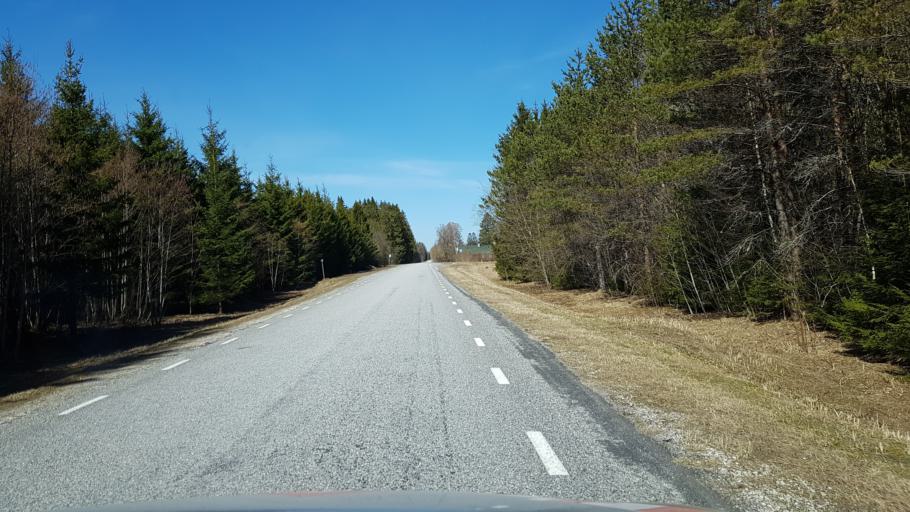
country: EE
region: Laeaene-Virumaa
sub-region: Vinni vald
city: Vinni
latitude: 59.1595
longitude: 26.5136
